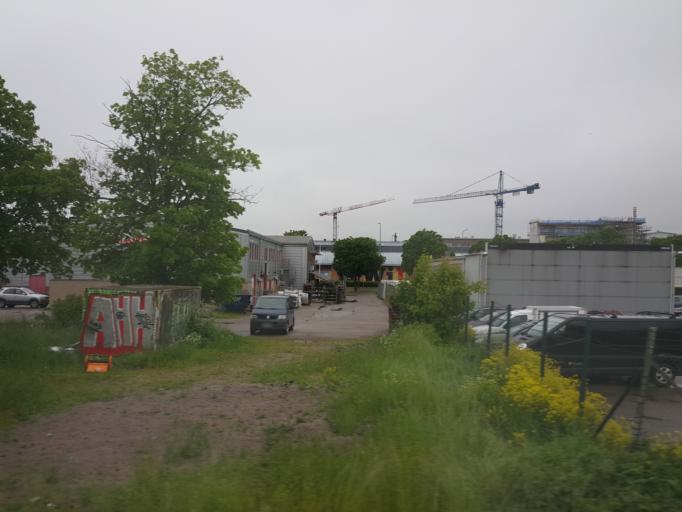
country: SE
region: Uppsala
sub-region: Uppsala Kommun
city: Uppsala
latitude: 59.8512
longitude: 17.6603
